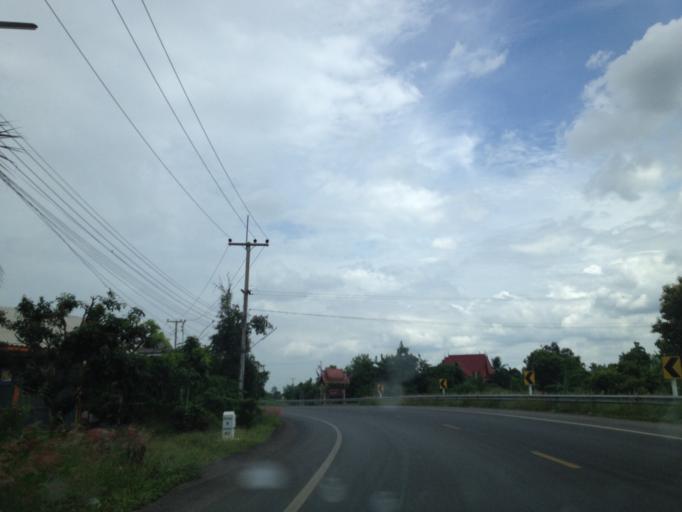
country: TH
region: Chiang Mai
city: San Pa Tong
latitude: 18.6343
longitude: 98.8548
